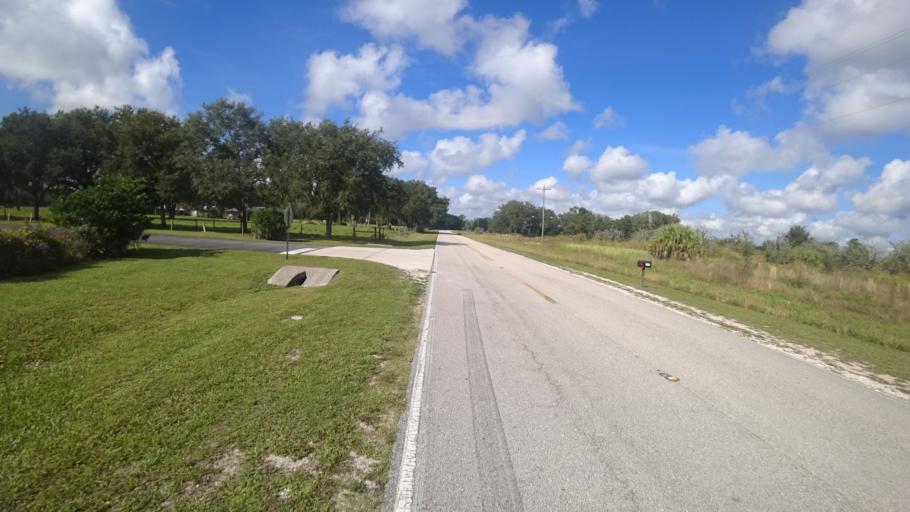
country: US
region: Florida
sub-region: Sarasota County
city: Lake Sarasota
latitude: 27.3393
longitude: -82.1995
